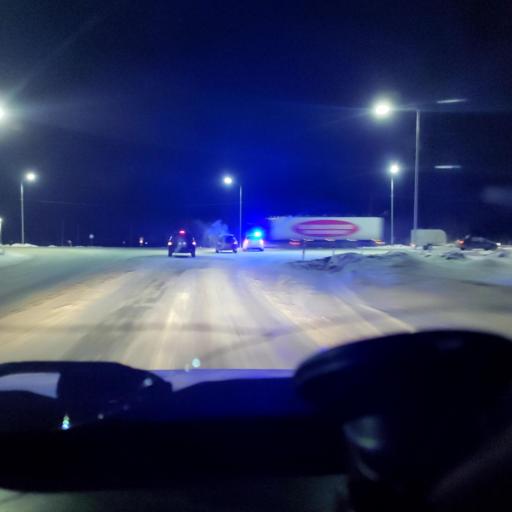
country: RU
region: Perm
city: Krasnokamsk
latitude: 58.1014
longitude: 55.7529
